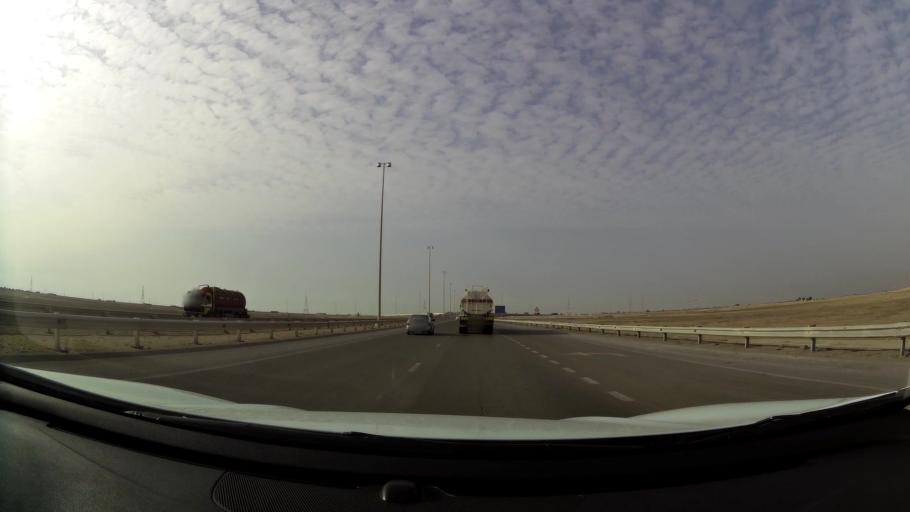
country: AE
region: Abu Dhabi
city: Abu Dhabi
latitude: 24.2070
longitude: 54.4184
